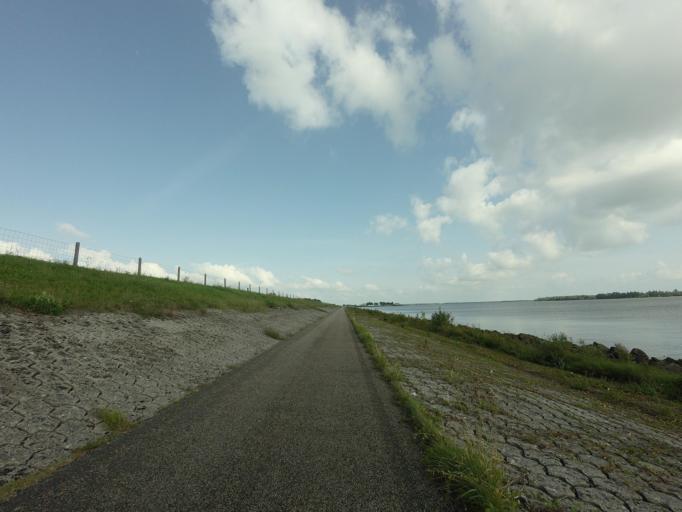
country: NL
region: Flevoland
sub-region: Gemeente Dronten
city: Dronten
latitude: 52.6129
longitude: 5.7288
